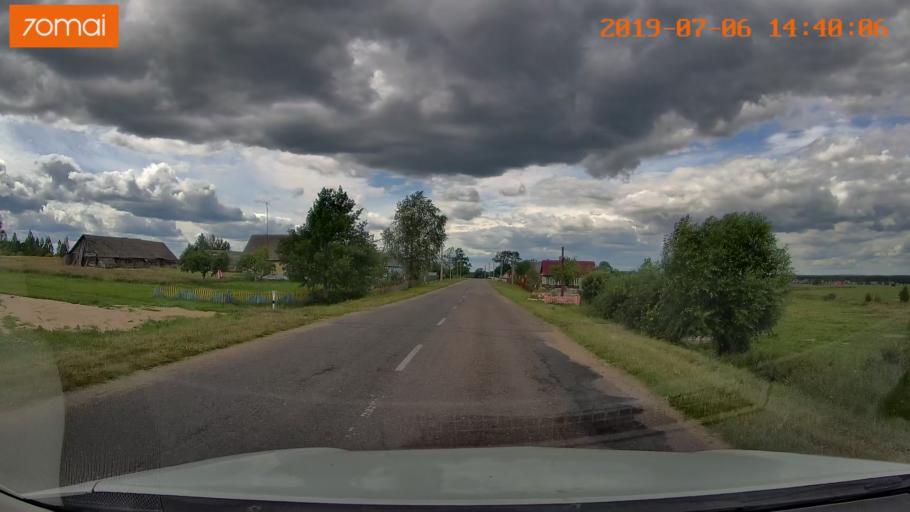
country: BY
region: Minsk
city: Ivyanyets
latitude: 53.9221
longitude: 26.6779
